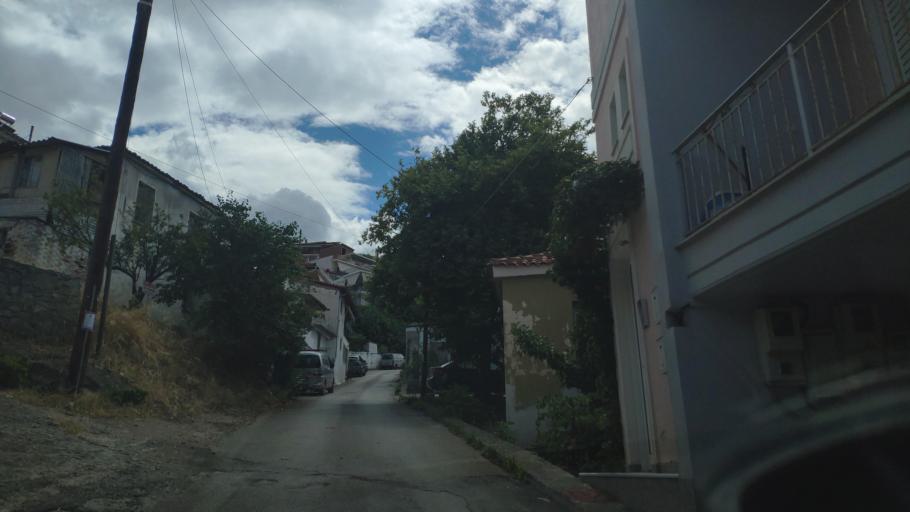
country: GR
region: Central Greece
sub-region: Nomos Voiotias
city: Livadeia
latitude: 38.4345
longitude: 22.8725
